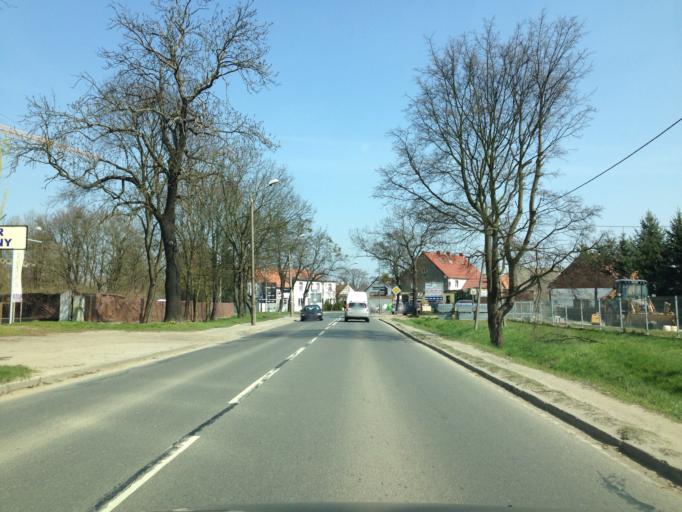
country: PL
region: Lower Silesian Voivodeship
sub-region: Powiat wroclawski
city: Wilczyce
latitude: 51.1142
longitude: 17.1259
